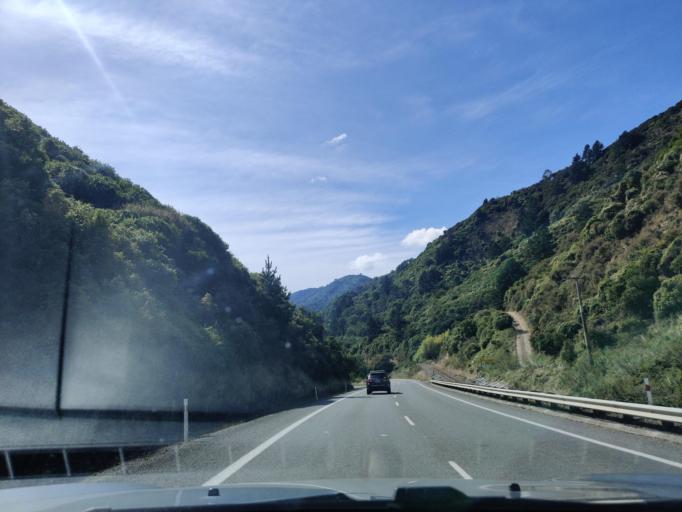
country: NZ
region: Marlborough
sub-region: Marlborough District
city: Picton
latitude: -41.3059
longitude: 173.9882
